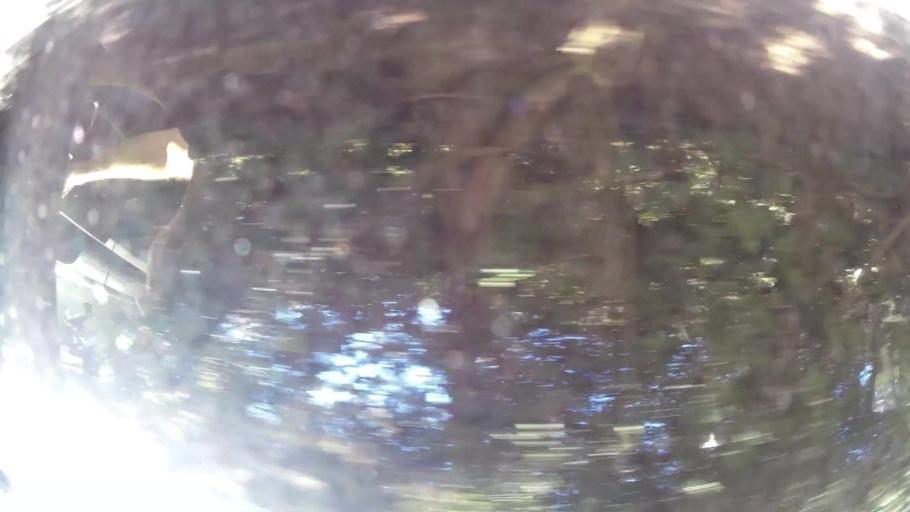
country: GT
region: Sacatepequez
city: Santa Lucia Milpas Altas
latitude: 14.5621
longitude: -90.7041
